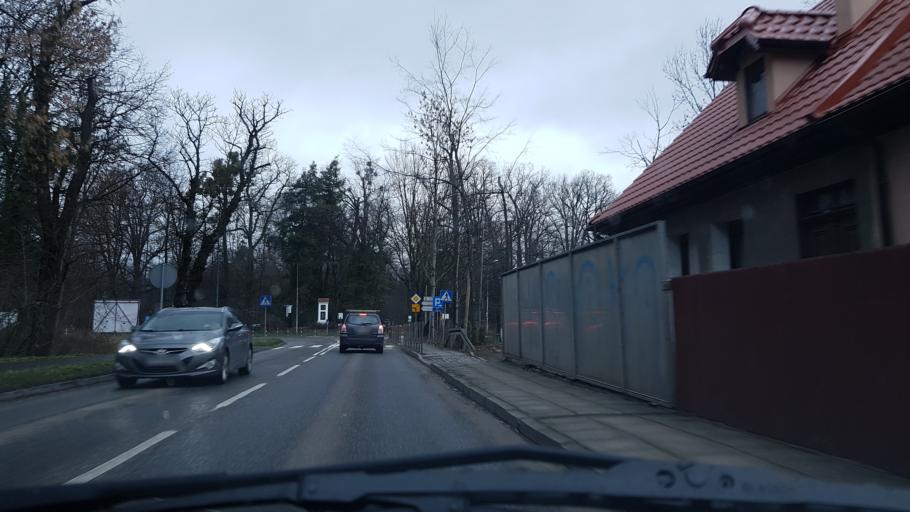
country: PL
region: Silesian Voivodeship
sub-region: Powiat pszczynski
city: Pszczyna
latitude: 49.9764
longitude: 18.9368
